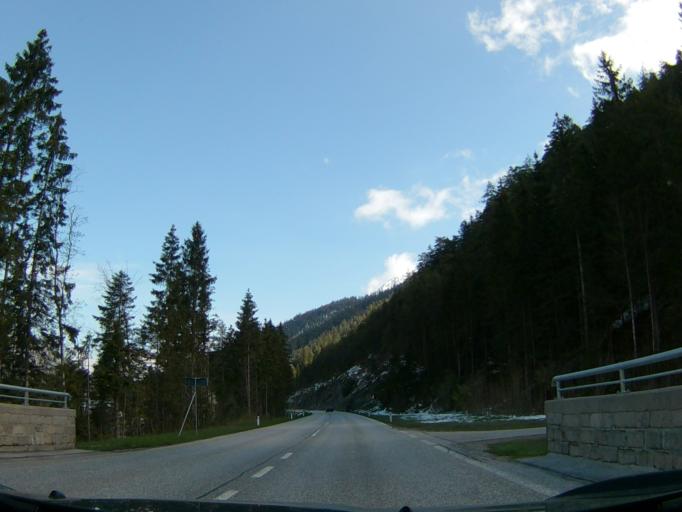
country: AT
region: Tyrol
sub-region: Politischer Bezirk Schwaz
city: Achenkirch
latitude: 47.4849
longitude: 11.7145
